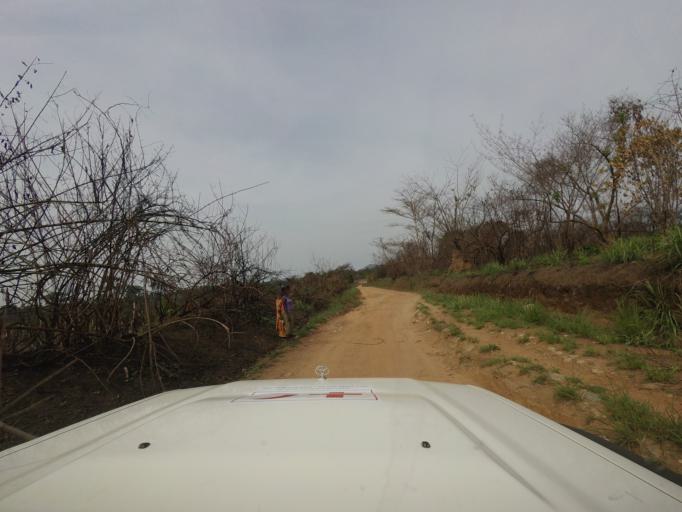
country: GN
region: Nzerekore
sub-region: Macenta
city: Macenta
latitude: 8.5165
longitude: -9.5215
